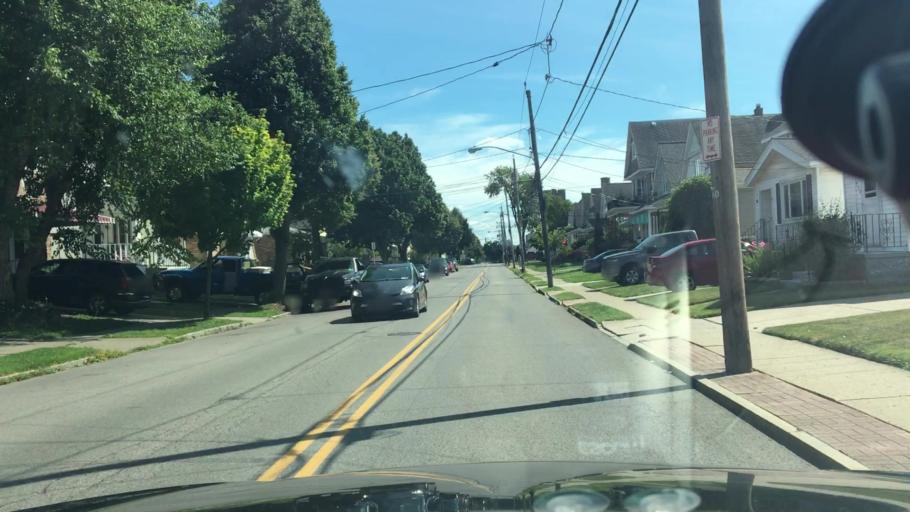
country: US
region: New York
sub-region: Erie County
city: Sloan
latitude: 42.8739
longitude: -78.8020
